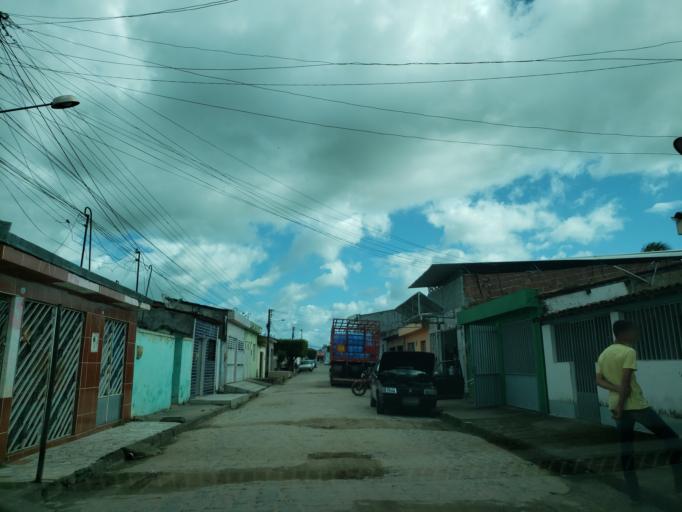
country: BR
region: Alagoas
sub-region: Uniao Dos Palmares
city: Uniao dos Palmares
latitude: -9.1626
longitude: -36.0223
